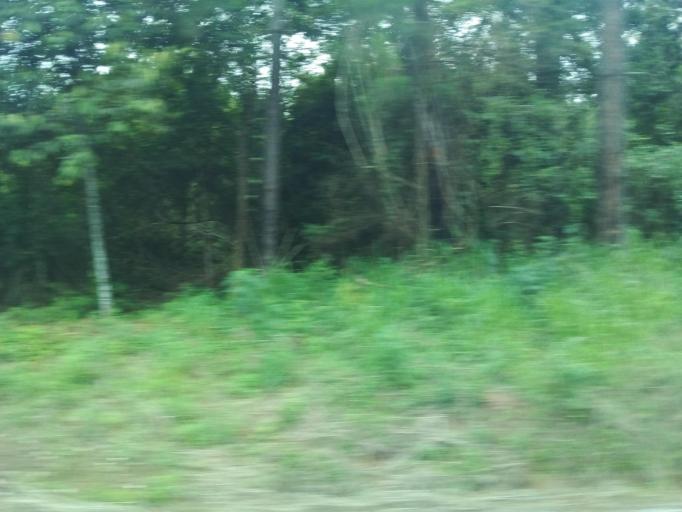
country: BR
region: Minas Gerais
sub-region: Rio Piracicaba
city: Rio Piracicaba
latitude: -19.9735
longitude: -43.2358
